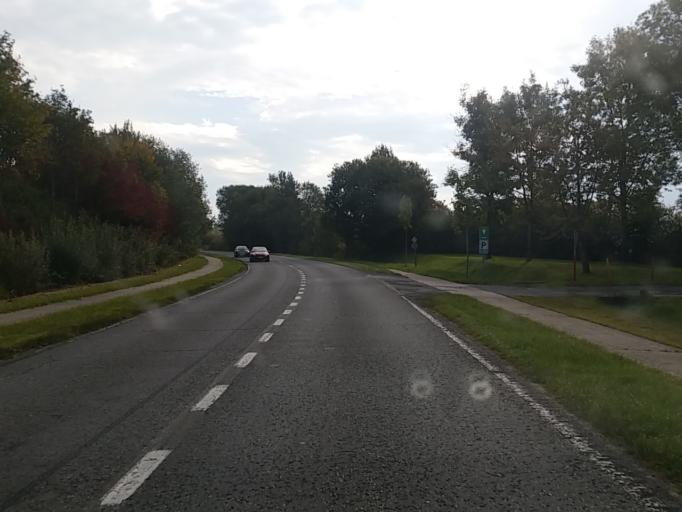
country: BE
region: Wallonia
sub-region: Province du Luxembourg
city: Tintigny
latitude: 49.6798
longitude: 5.5276
